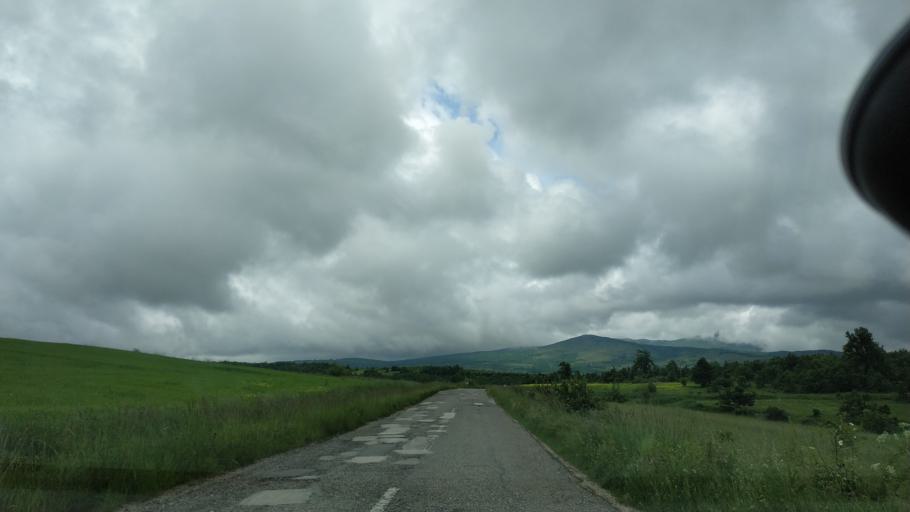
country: RS
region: Central Serbia
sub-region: Zajecarski Okrug
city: Soko Banja
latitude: 43.7009
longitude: 21.9365
